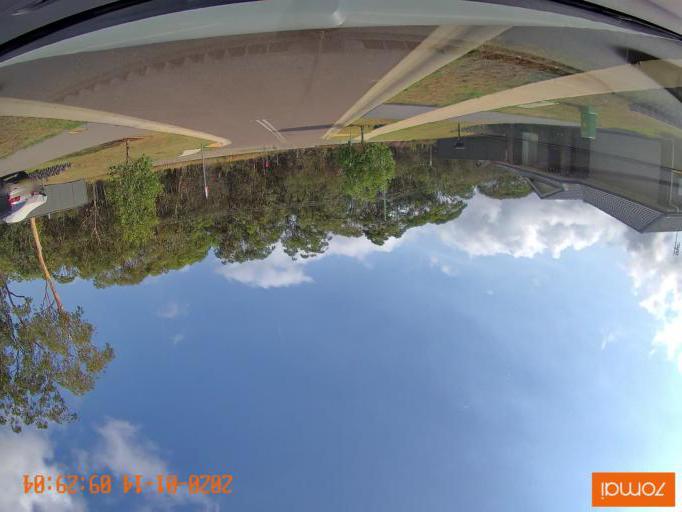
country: AU
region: New South Wales
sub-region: Lake Macquarie Shire
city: Dora Creek
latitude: -33.1202
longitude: 151.5287
